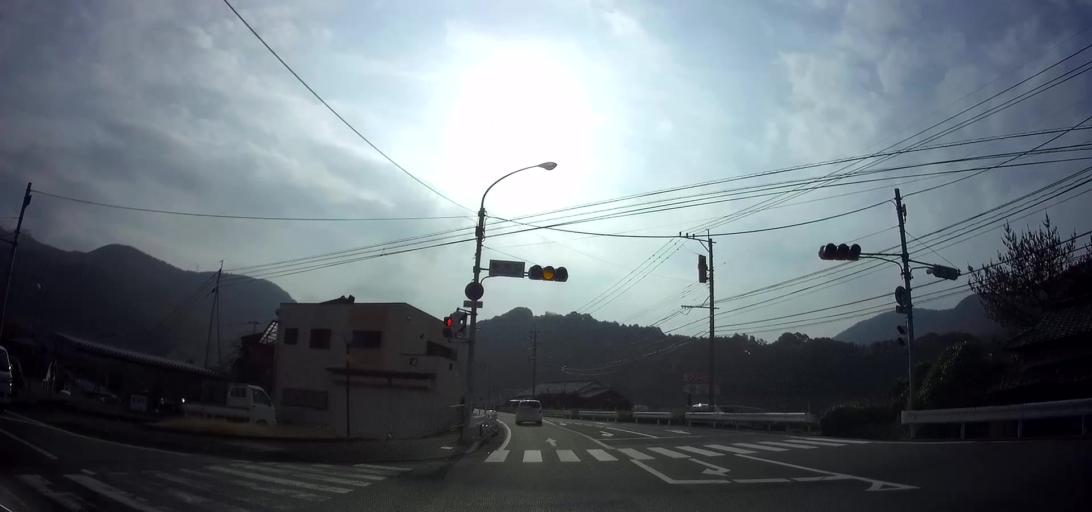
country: JP
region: Nagasaki
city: Shimabara
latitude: 32.7822
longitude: 130.2057
